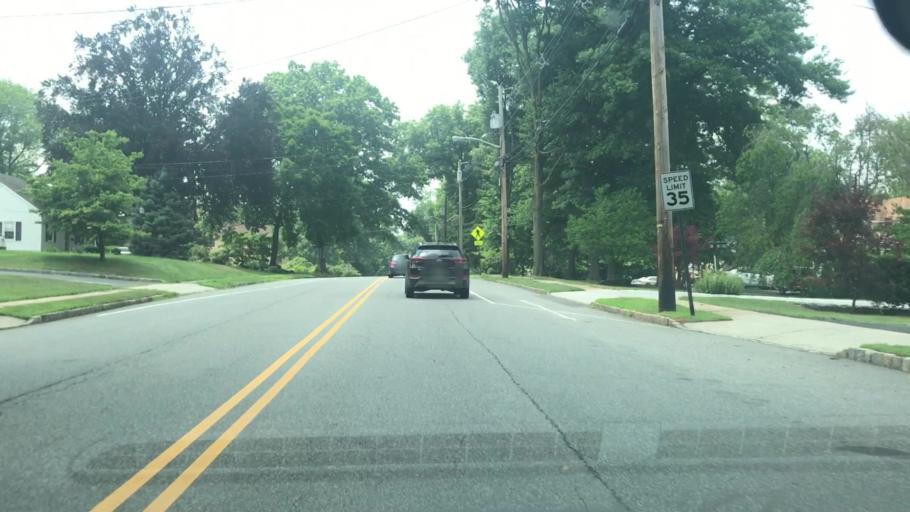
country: US
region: New Jersey
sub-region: Union County
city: Clark
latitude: 40.6117
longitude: -74.3329
